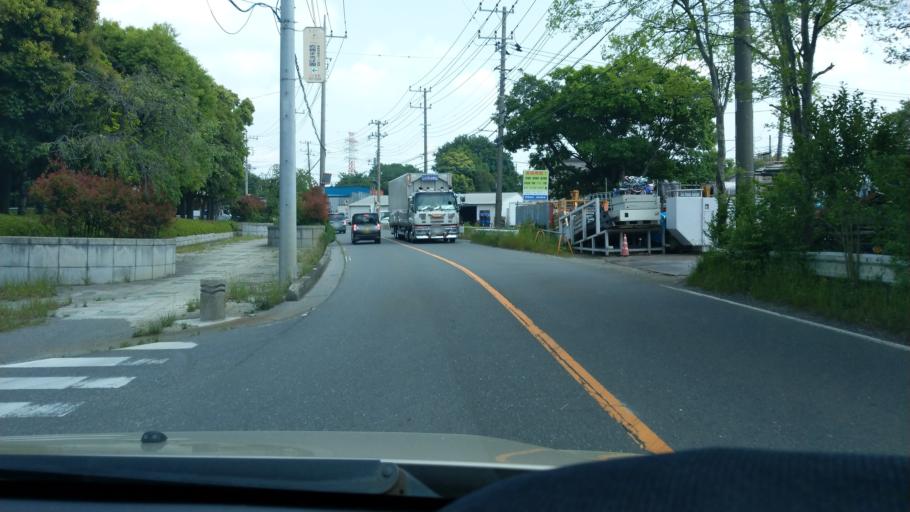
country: JP
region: Saitama
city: Iwatsuki
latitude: 35.9157
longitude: 139.7160
